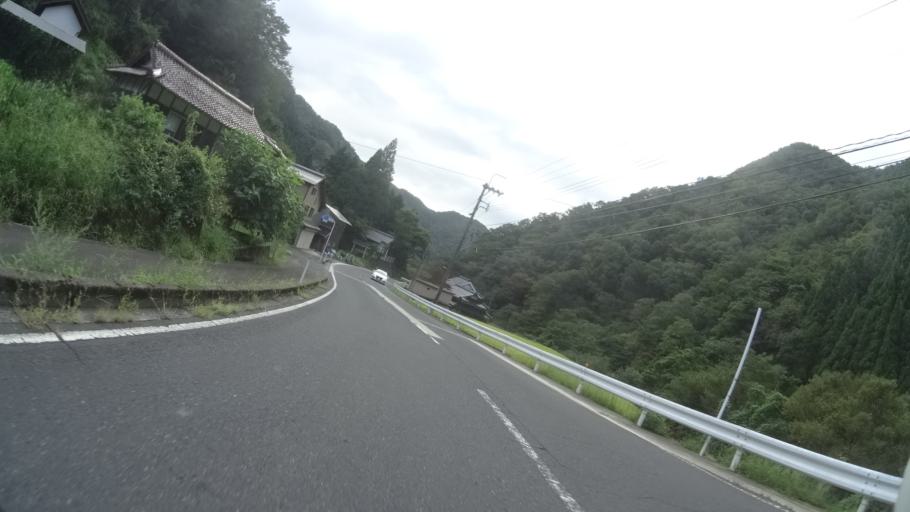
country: JP
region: Tottori
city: Kurayoshi
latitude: 35.4011
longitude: 133.9492
